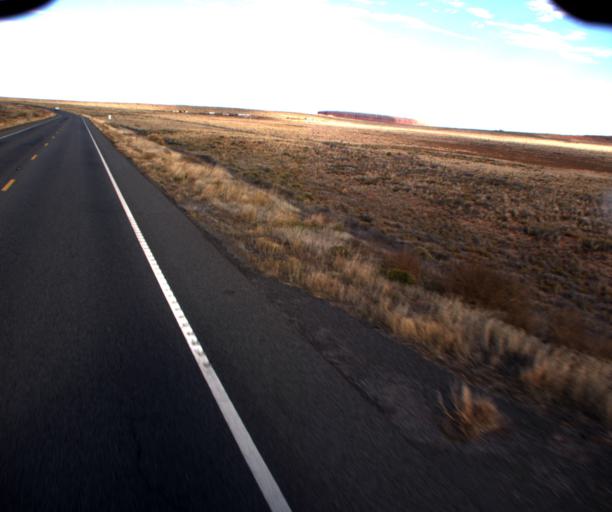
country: US
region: Arizona
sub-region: Apache County
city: Lukachukai
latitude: 36.9567
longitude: -109.3028
